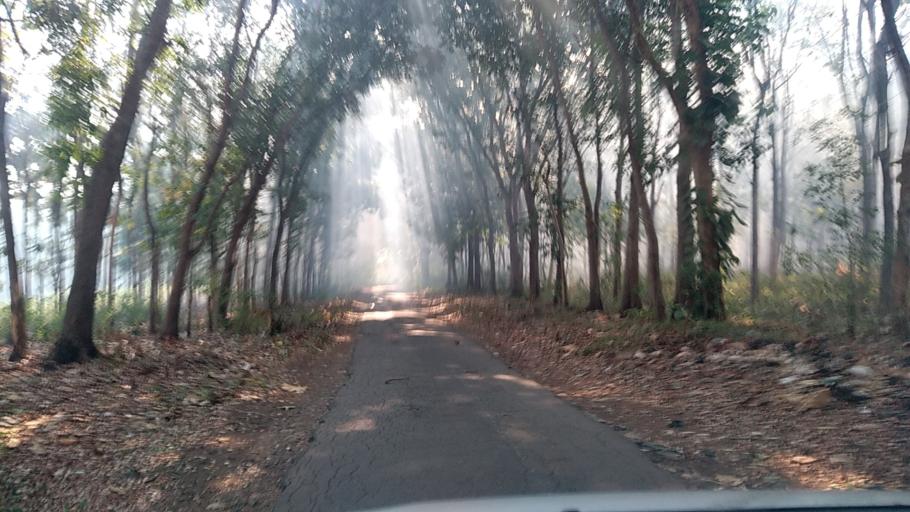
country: ID
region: Central Java
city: Semarang
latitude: -7.0198
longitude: 110.3284
